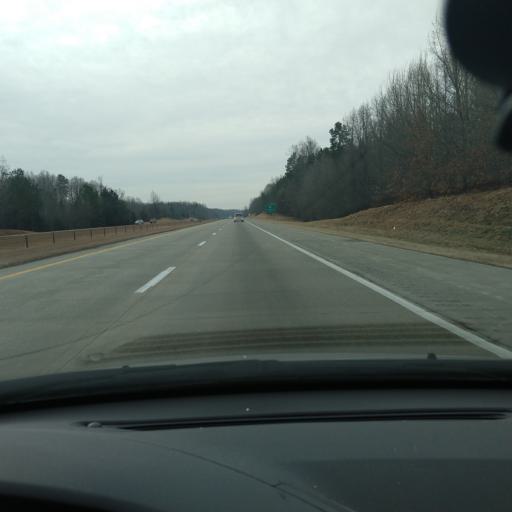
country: US
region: North Carolina
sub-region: Davidson County
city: Welcome
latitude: 35.8987
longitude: -80.2337
